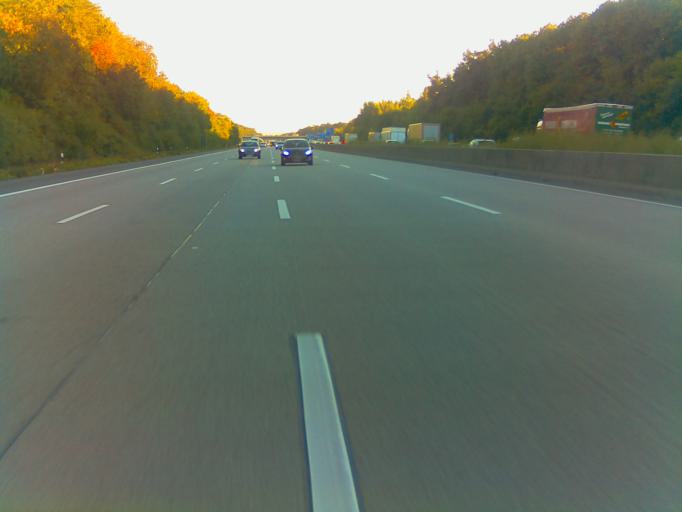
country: DE
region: Hesse
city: Morfelden-Walldorf
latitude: 49.9928
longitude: 8.5993
